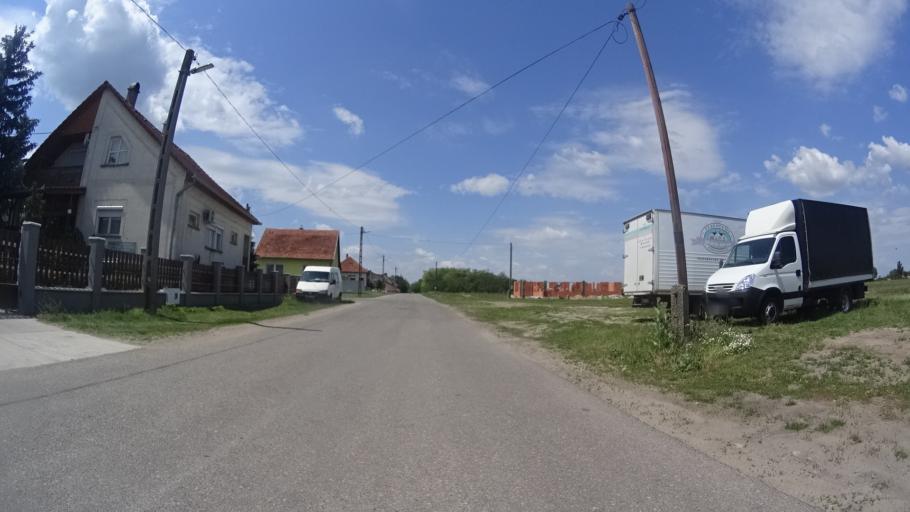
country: HU
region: Bacs-Kiskun
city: Tiszakecske
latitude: 46.9461
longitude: 20.0916
